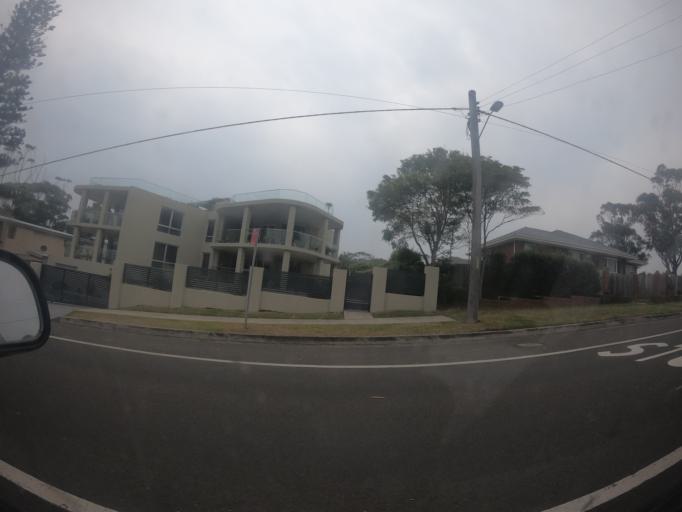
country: AU
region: New South Wales
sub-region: Shellharbour
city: Shellharbour Village
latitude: -34.5771
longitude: 150.8694
